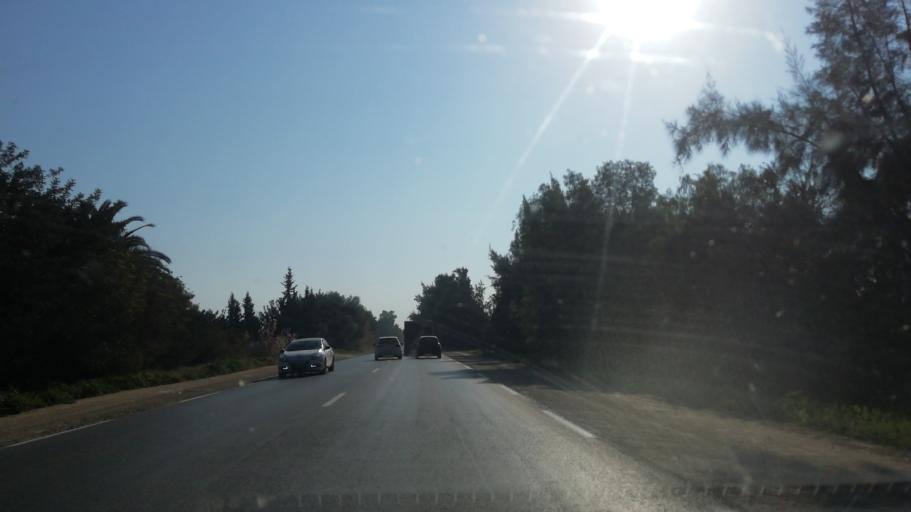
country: DZ
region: Relizane
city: Relizane
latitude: 35.7297
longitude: 0.4744
